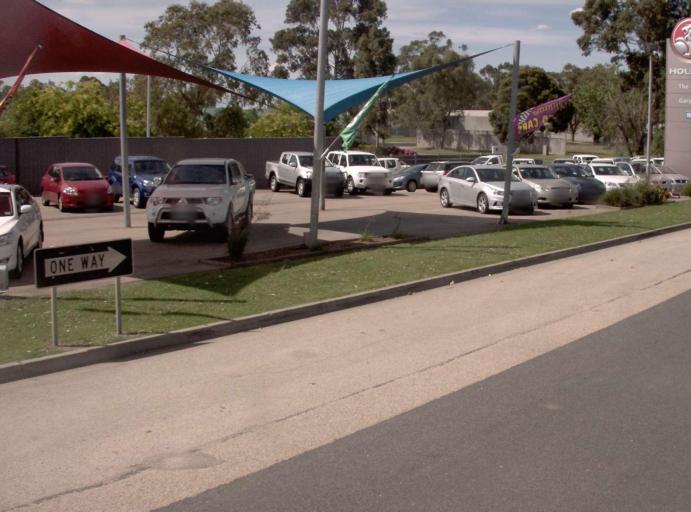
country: AU
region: Victoria
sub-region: East Gippsland
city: Bairnsdale
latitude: -37.8383
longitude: 147.5958
